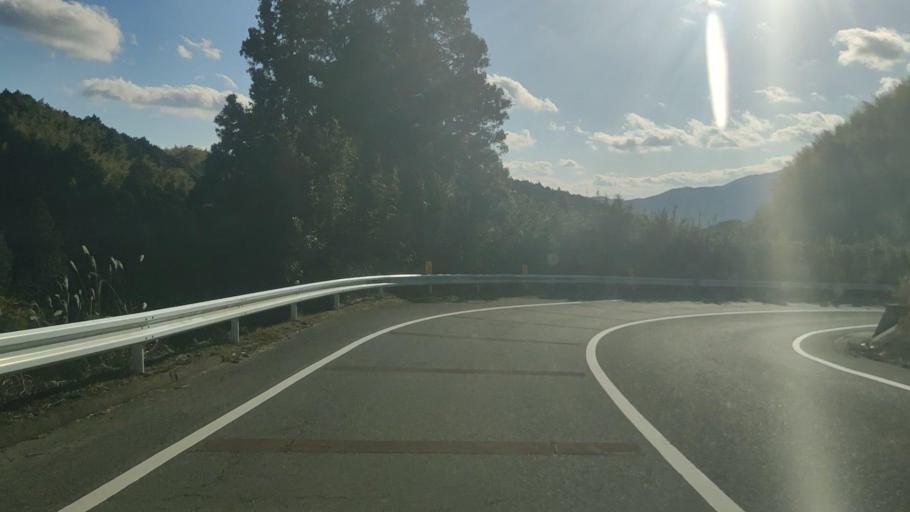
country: JP
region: Saga Prefecture
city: Kanzakimachi-kanzaki
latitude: 33.3917
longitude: 130.2675
